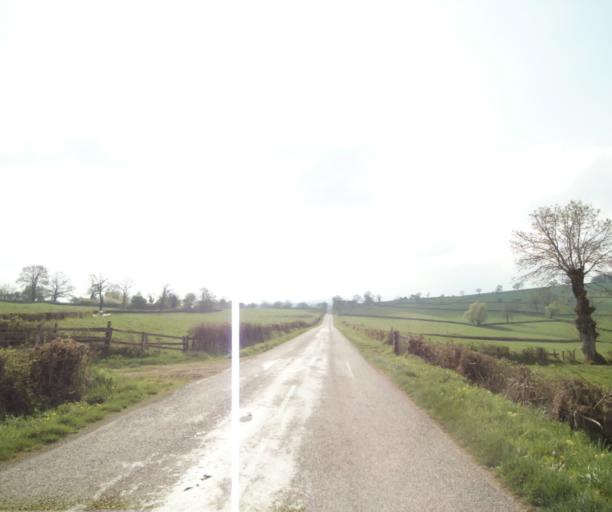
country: FR
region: Bourgogne
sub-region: Departement de Saone-et-Loire
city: Charolles
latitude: 46.3894
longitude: 4.2395
